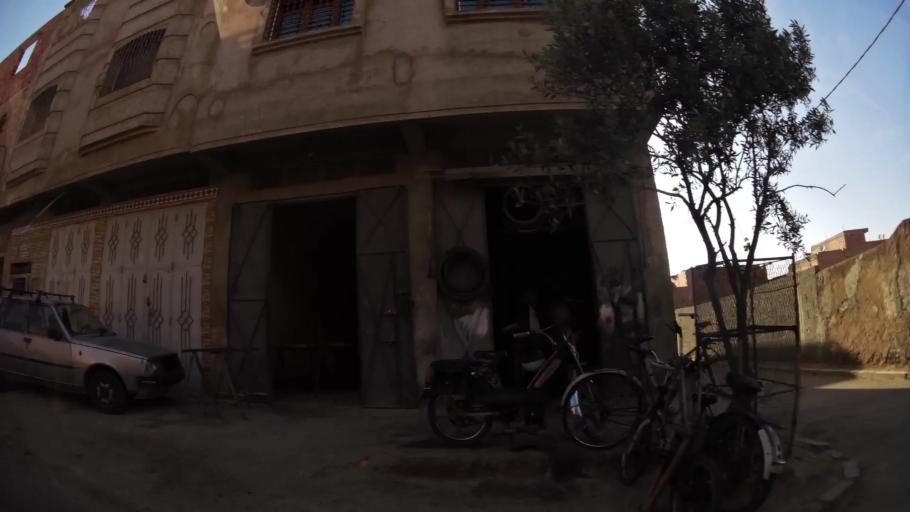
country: MA
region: Oriental
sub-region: Oujda-Angad
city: Oujda
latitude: 34.7170
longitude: -1.9056
